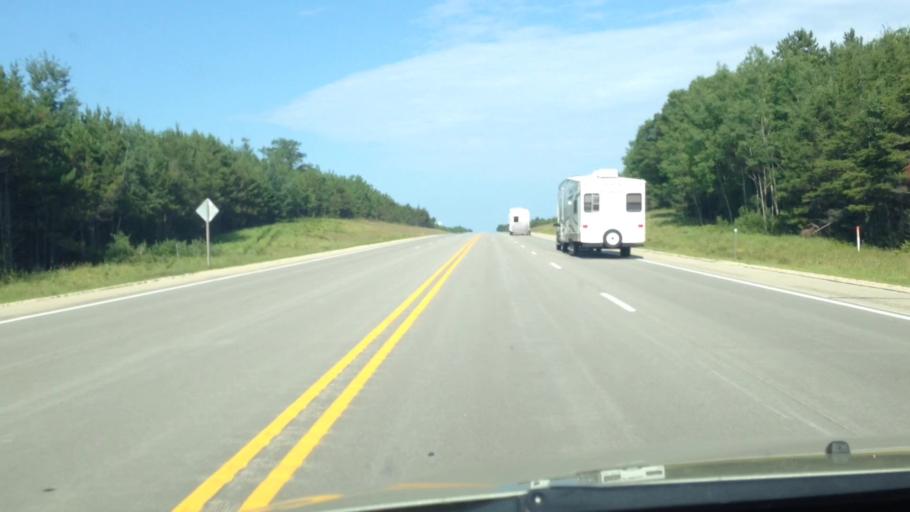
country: US
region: Michigan
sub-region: Schoolcraft County
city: Manistique
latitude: 45.9072
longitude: -86.4159
